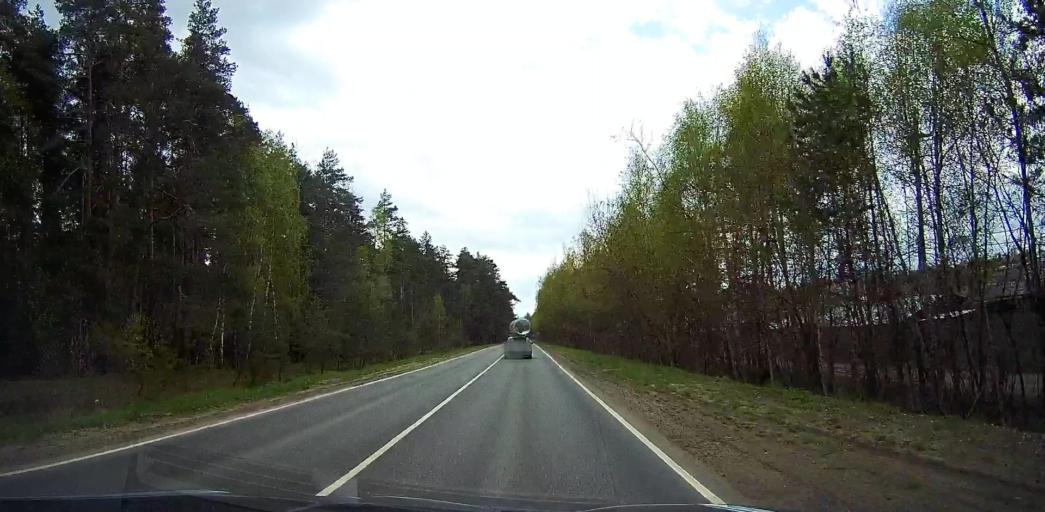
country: RU
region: Moskovskaya
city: Beloozerskiy
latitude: 55.4951
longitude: 38.4292
